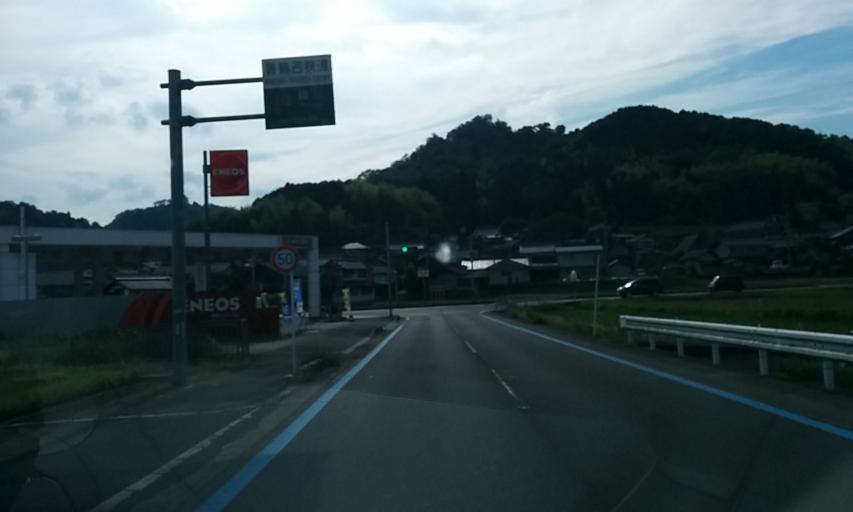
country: JP
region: Kyoto
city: Ayabe
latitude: 35.3191
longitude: 135.2622
